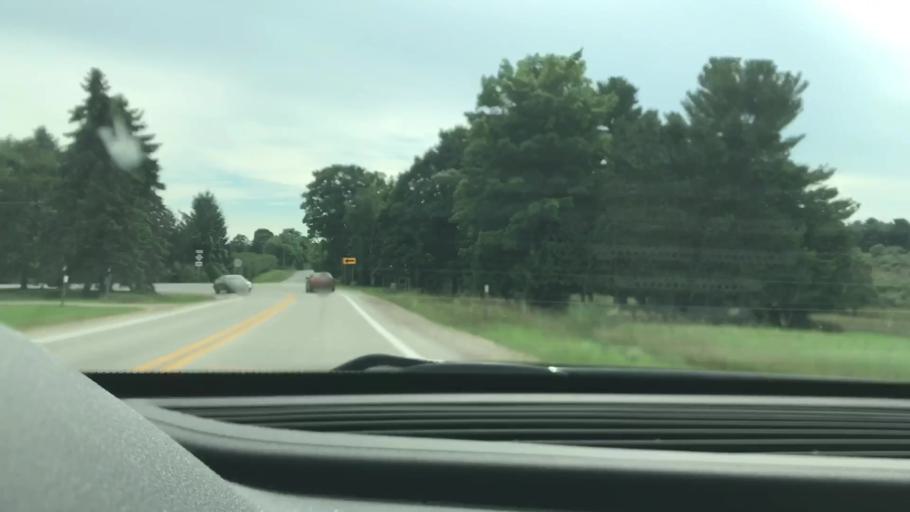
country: US
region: Michigan
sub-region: Antrim County
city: Bellaire
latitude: 45.0997
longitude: -85.3052
